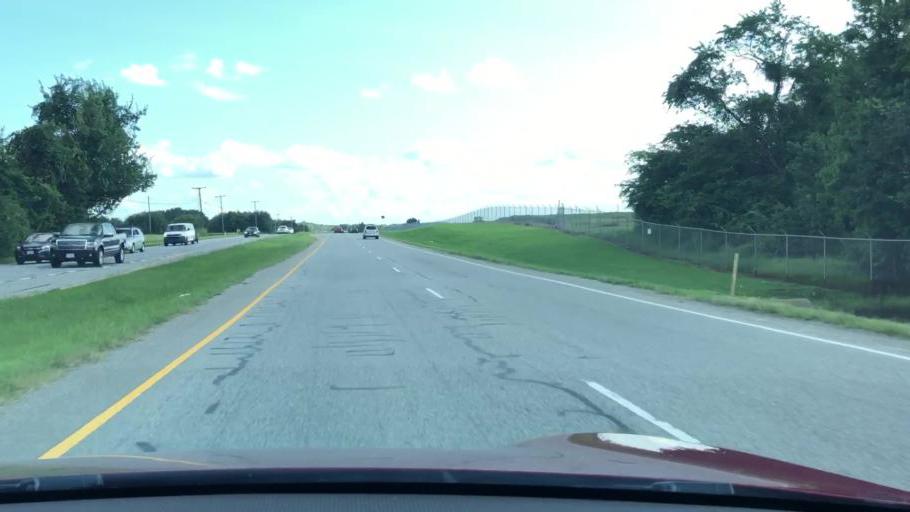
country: US
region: Virginia
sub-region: City of Virginia Beach
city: Virginia Beach
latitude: 36.8261
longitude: -76.0099
